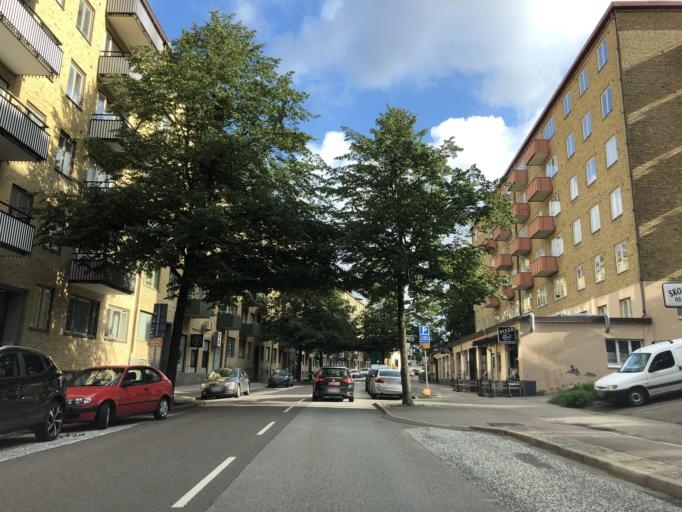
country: SE
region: Vaestra Goetaland
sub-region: Goteborg
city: Goeteborg
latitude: 57.7128
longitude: 11.9997
